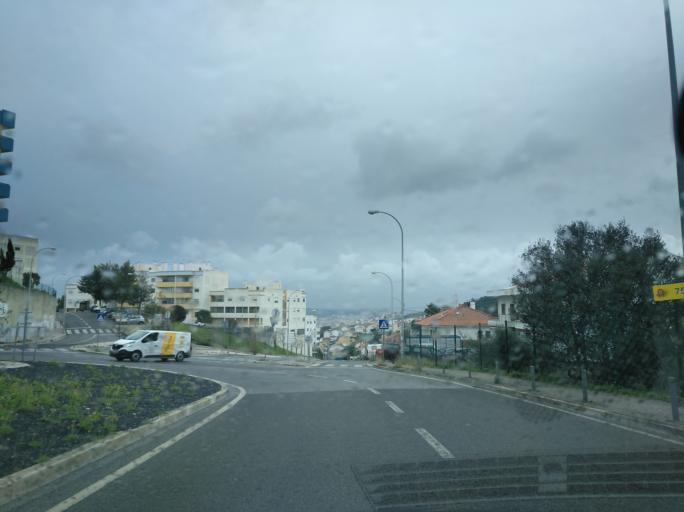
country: PT
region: Lisbon
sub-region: Odivelas
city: Famoes
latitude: 38.7917
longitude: -9.2281
